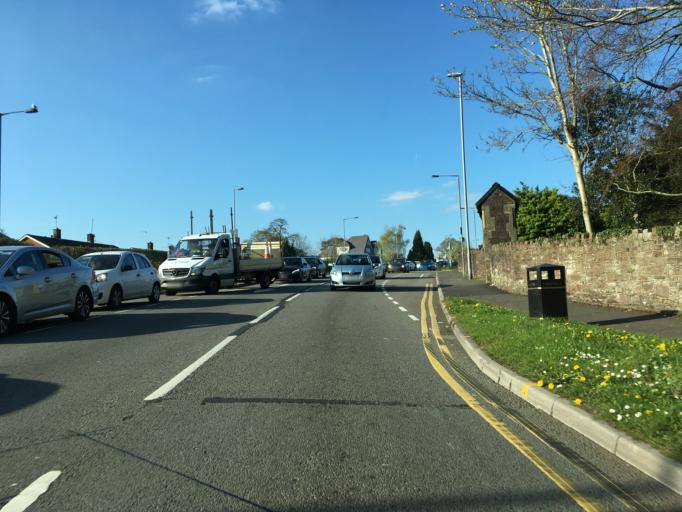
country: GB
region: Wales
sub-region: Newport
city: Newport
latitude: 51.6060
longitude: -3.0087
